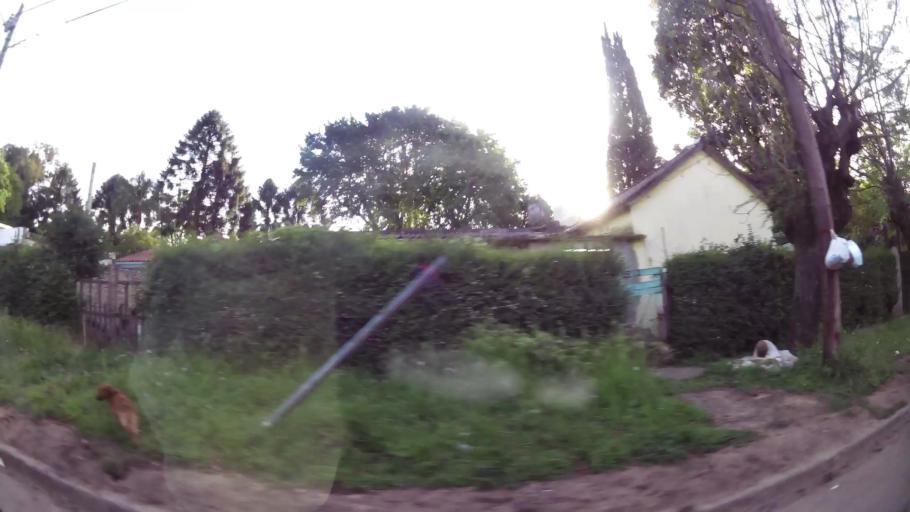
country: AR
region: Buenos Aires
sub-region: Partido de Almirante Brown
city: Adrogue
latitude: -34.7975
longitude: -58.3520
